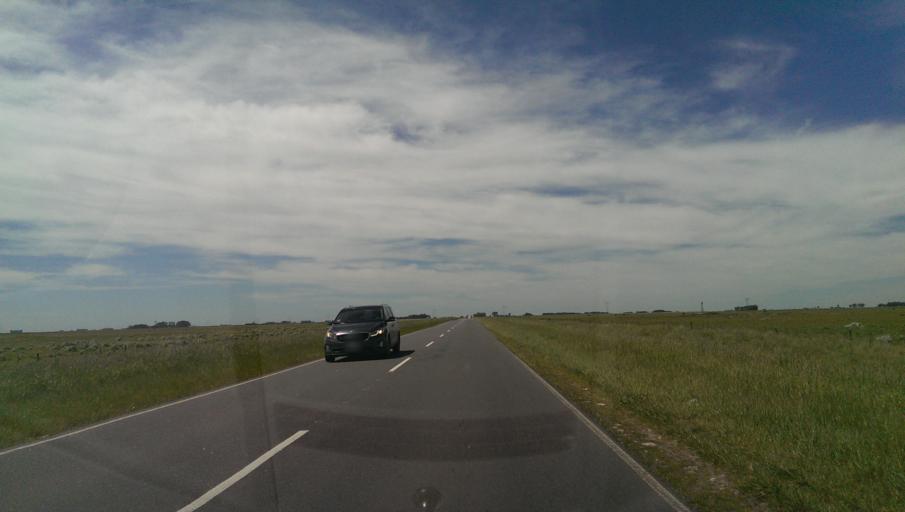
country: AR
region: Buenos Aires
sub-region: Partido de Laprida
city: Laprida
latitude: -37.2387
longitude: -60.7500
